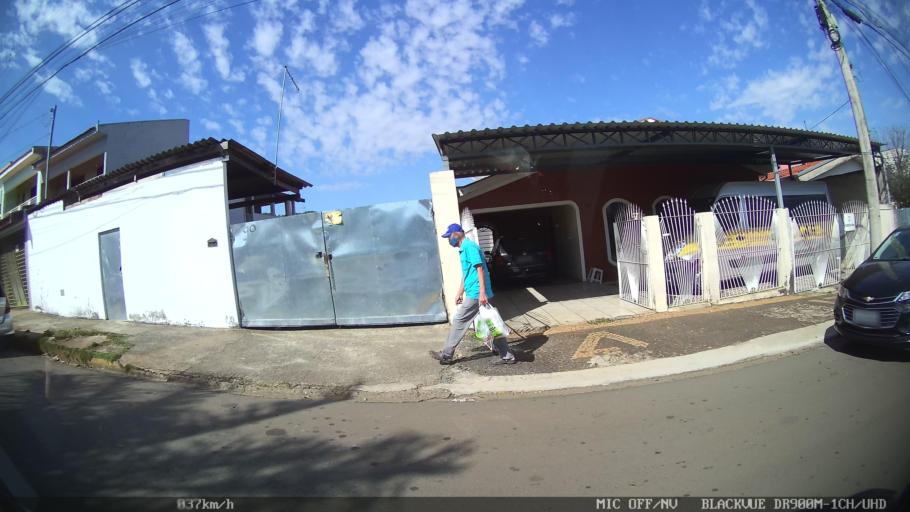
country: BR
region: Sao Paulo
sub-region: Americana
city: Americana
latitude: -22.7395
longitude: -47.3018
